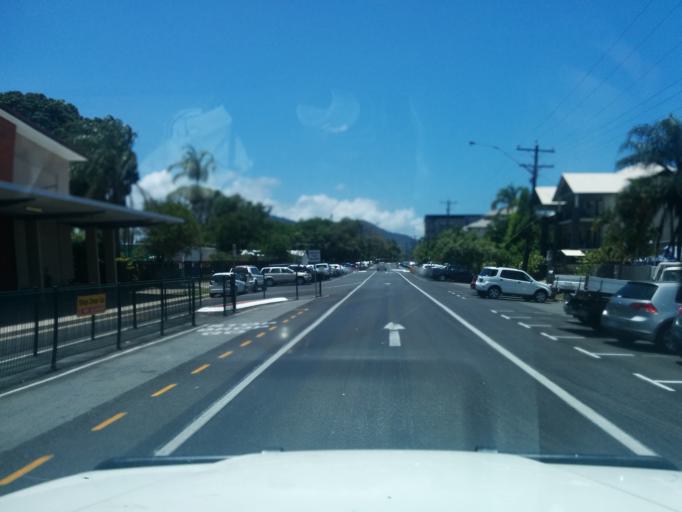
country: AU
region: Queensland
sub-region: Cairns
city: Cairns
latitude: -16.9148
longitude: 145.7679
